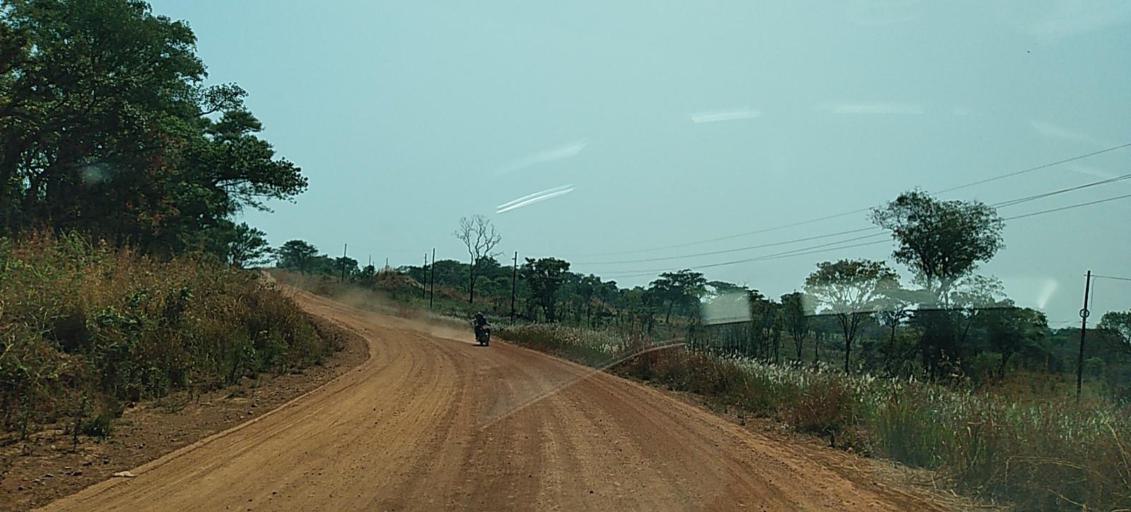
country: ZM
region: North-Western
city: Kansanshi
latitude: -12.0073
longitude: 26.5783
